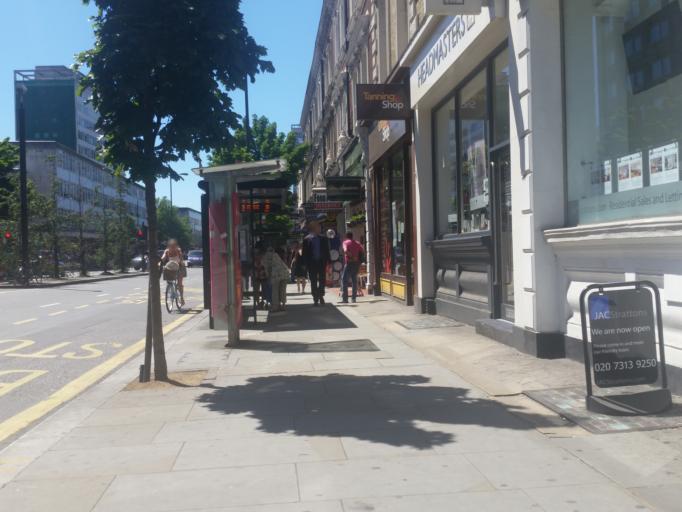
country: GB
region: England
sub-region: Greater London
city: Bayswater
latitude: 51.5097
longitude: -0.1930
